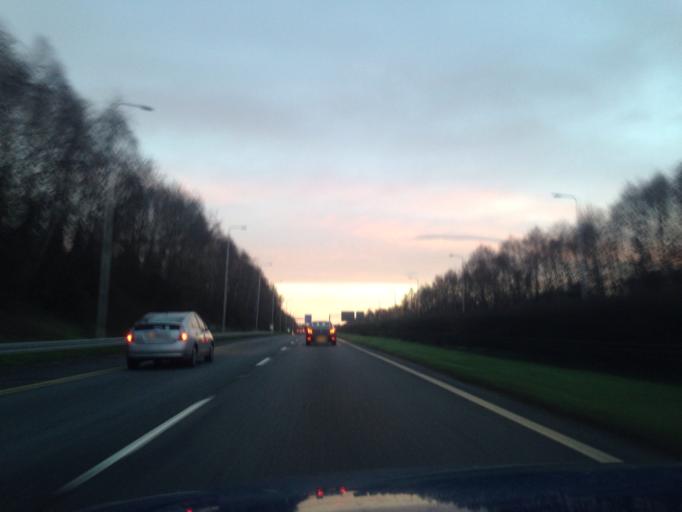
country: IE
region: Leinster
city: Little Bray
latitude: 53.2020
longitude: -6.1303
